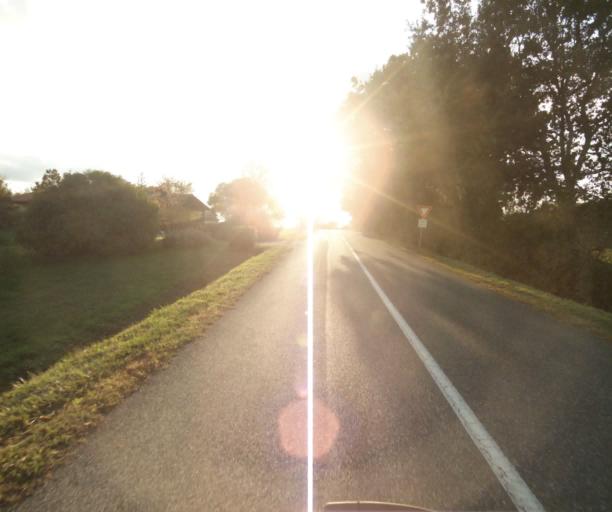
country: FR
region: Midi-Pyrenees
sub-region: Departement du Tarn-et-Garonne
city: Verdun-sur-Garonne
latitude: 43.8346
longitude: 1.1622
